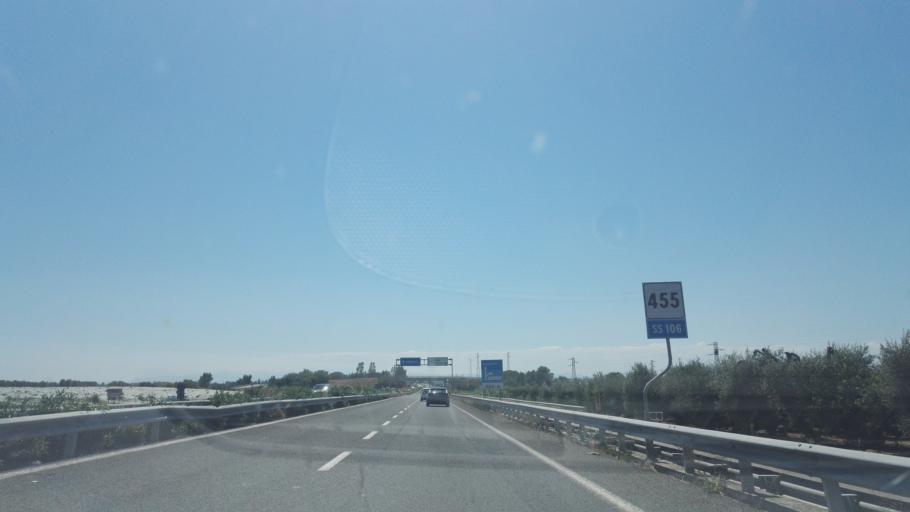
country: IT
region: Apulia
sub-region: Provincia di Taranto
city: Marina di Ginosa
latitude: 40.4364
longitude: 16.8389
